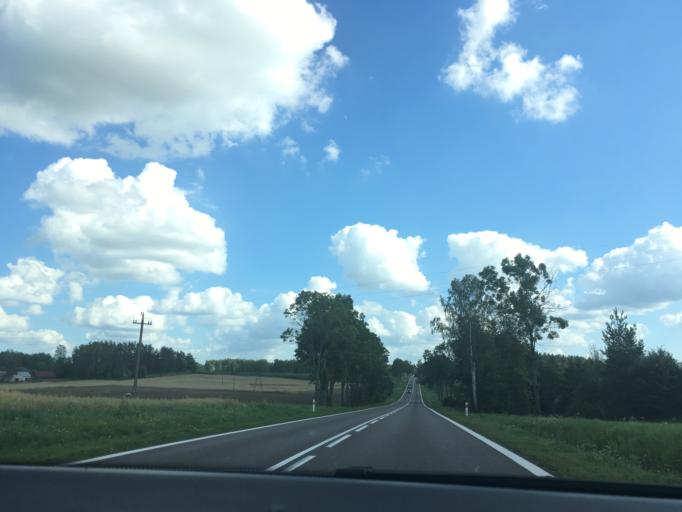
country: PL
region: Podlasie
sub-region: Powiat sokolski
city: Janow
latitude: 53.4174
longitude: 23.1140
